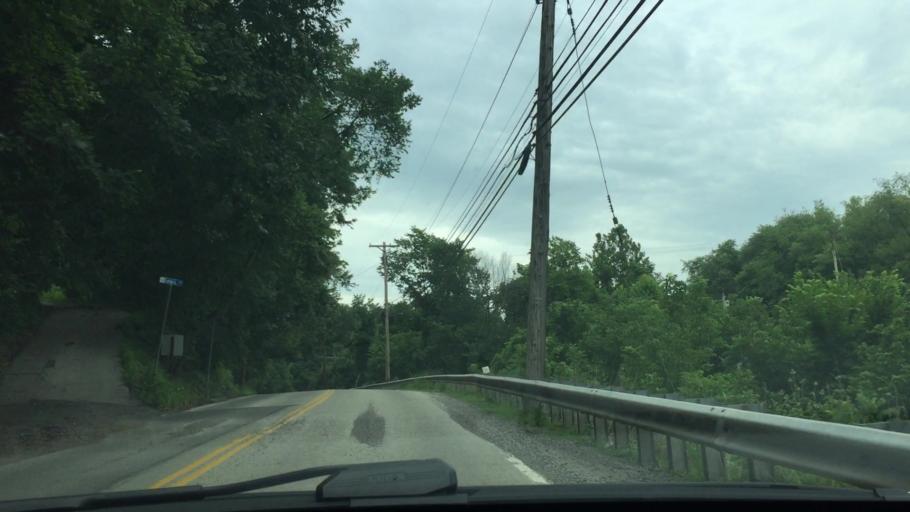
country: US
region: Pennsylvania
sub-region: Allegheny County
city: Rennerdale
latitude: 40.3777
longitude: -80.1430
